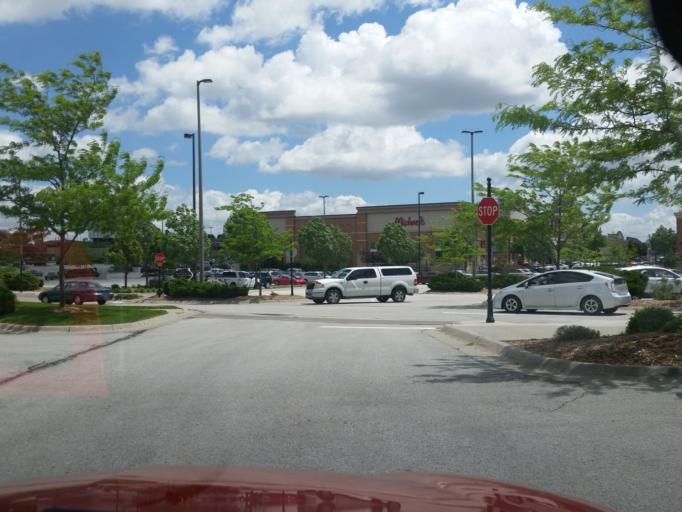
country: US
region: Nebraska
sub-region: Sarpy County
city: Papillion
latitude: 41.1368
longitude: -96.0302
